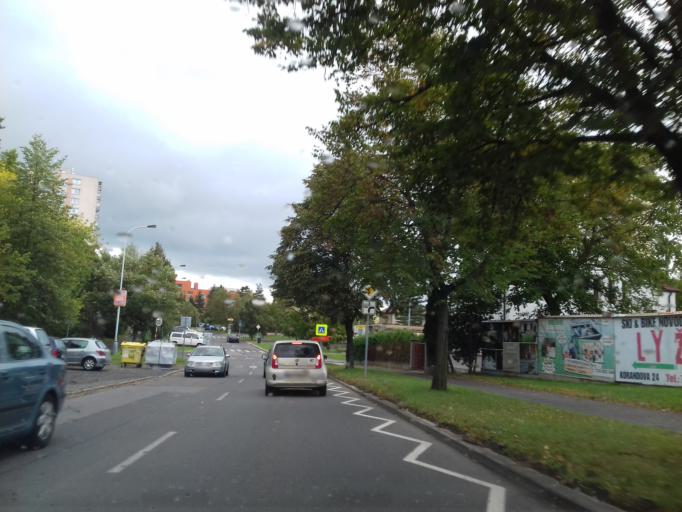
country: CZ
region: Praha
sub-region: Praha 4
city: Hodkovicky
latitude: 50.0257
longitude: 14.4266
